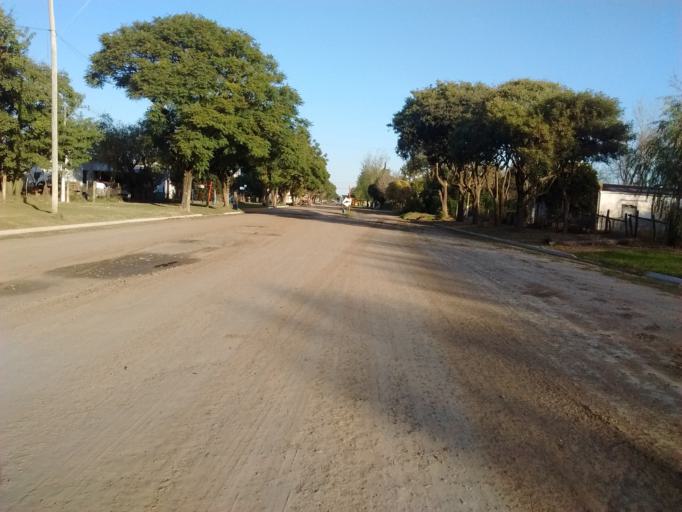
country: AR
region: Santa Fe
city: Galvez
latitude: -32.1665
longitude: -61.1600
